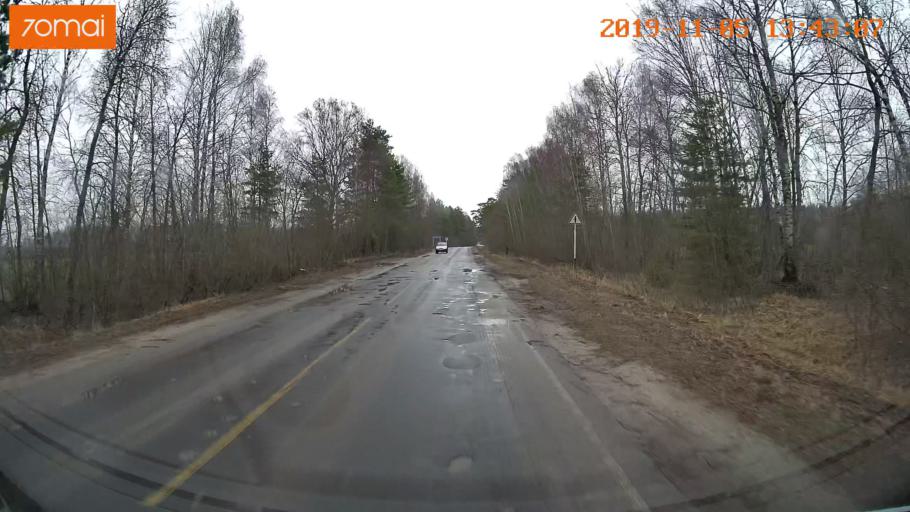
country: RU
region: Ivanovo
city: Shuya
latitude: 56.9714
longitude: 41.4004
